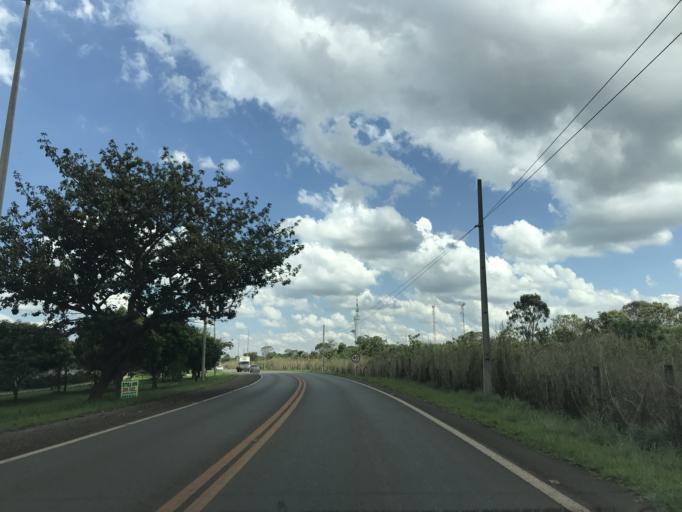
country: BR
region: Federal District
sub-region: Brasilia
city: Brasilia
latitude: -15.6870
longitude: -47.8372
